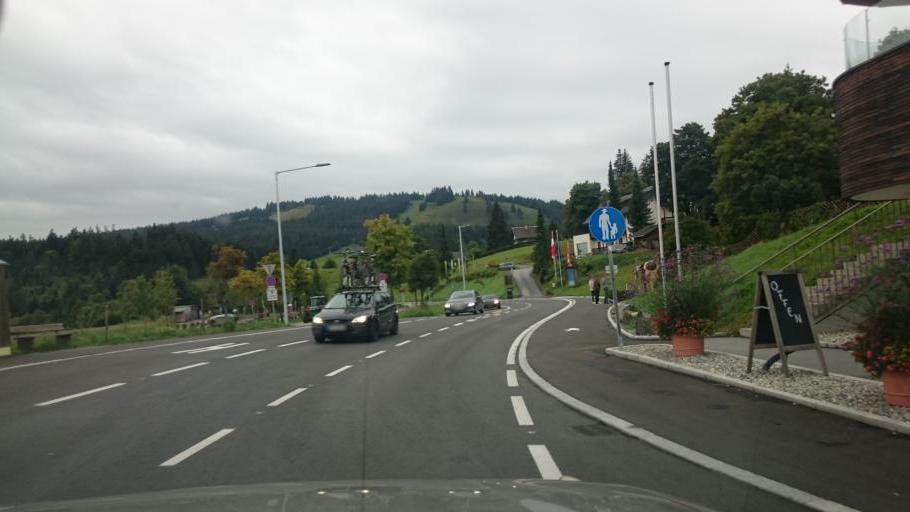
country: AT
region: Vorarlberg
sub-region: Politischer Bezirk Bregenz
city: Bildstein
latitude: 47.4233
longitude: 9.8091
